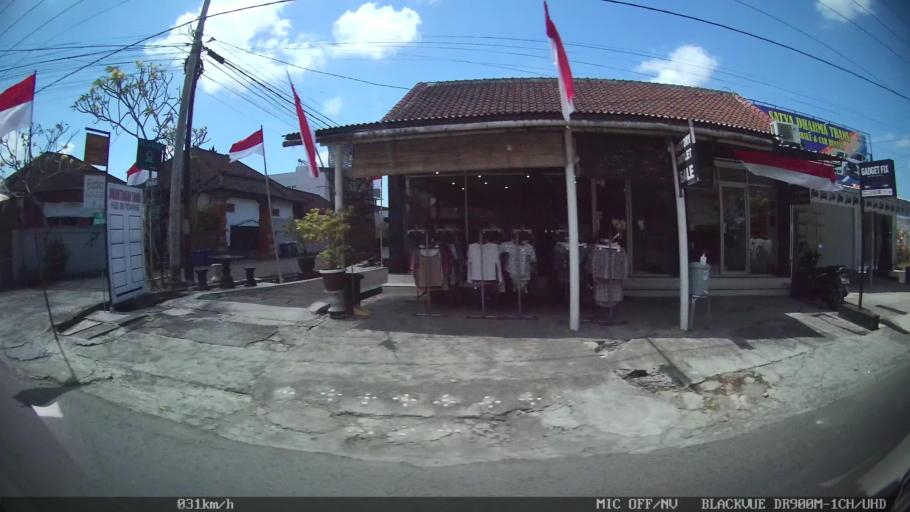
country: ID
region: Bali
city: Banjar Gunungpande
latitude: -8.6588
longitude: 115.1529
